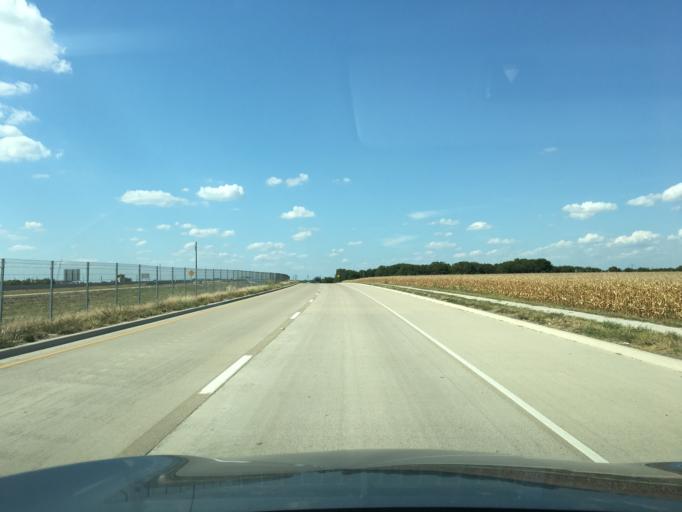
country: US
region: Texas
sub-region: Tarrant County
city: Mansfield
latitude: 32.5409
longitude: -97.0809
